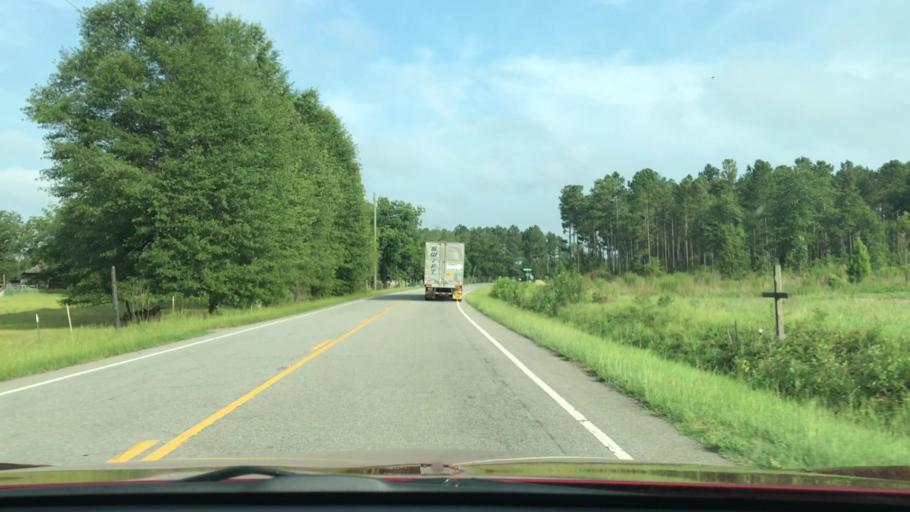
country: US
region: South Carolina
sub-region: Barnwell County
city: Williston
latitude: 33.6138
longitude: -81.2824
